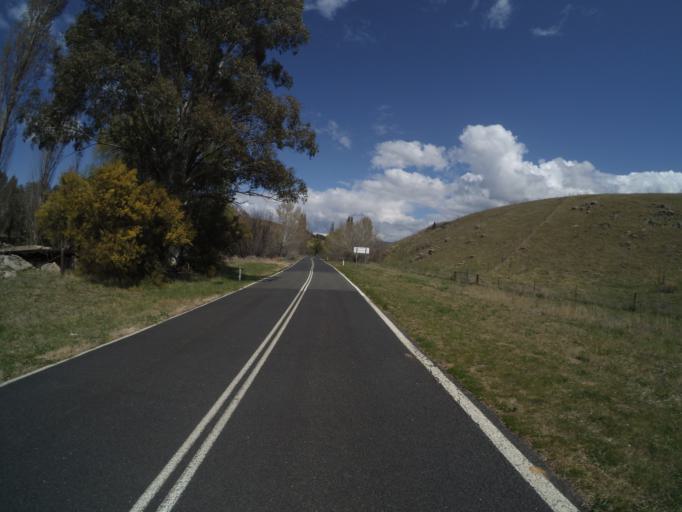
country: AU
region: Australian Capital Territory
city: Macarthur
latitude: -35.3990
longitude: 148.9603
